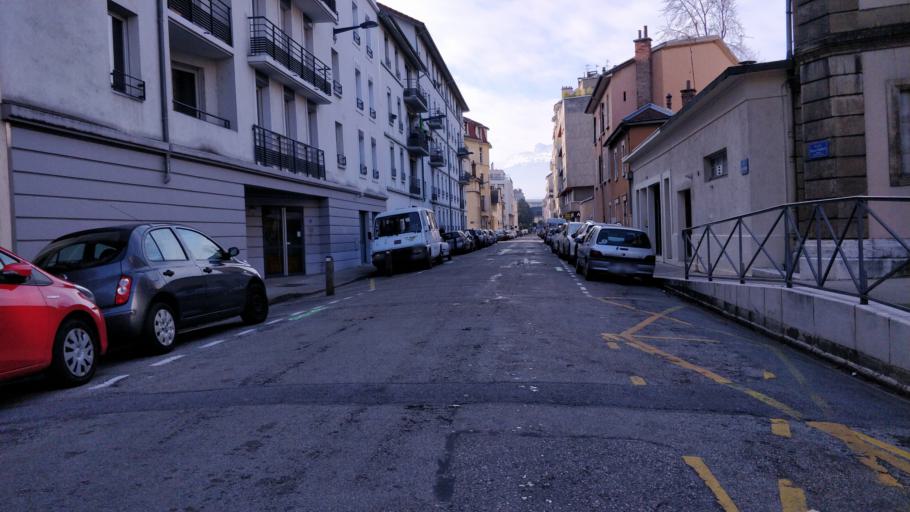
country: FR
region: Rhone-Alpes
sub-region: Departement de l'Isere
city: La Tronche
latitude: 45.1902
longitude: 5.7363
